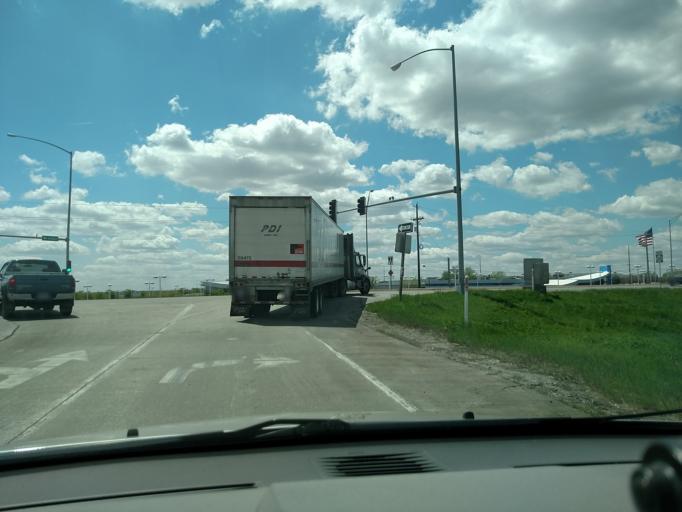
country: US
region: Iowa
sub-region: Polk County
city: Ankeny
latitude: 41.7033
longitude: -93.5779
